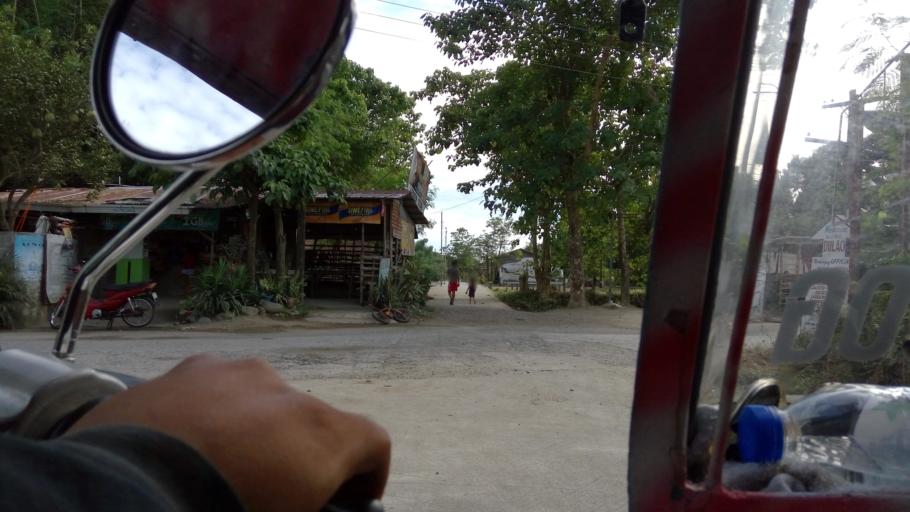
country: PH
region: Ilocos
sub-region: Province of La Union
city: San Eugenio
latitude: 16.3653
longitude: 120.3525
